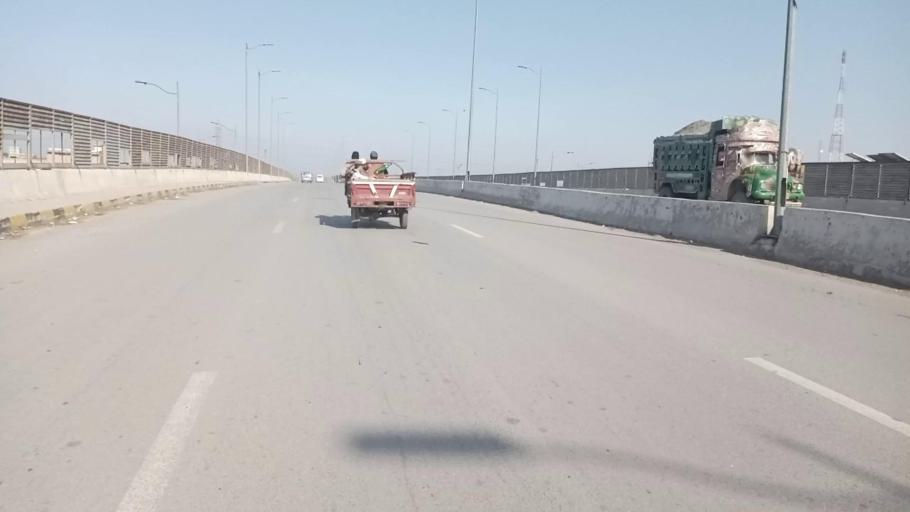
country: PK
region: Khyber Pakhtunkhwa
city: Peshawar
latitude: 34.0307
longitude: 71.5533
